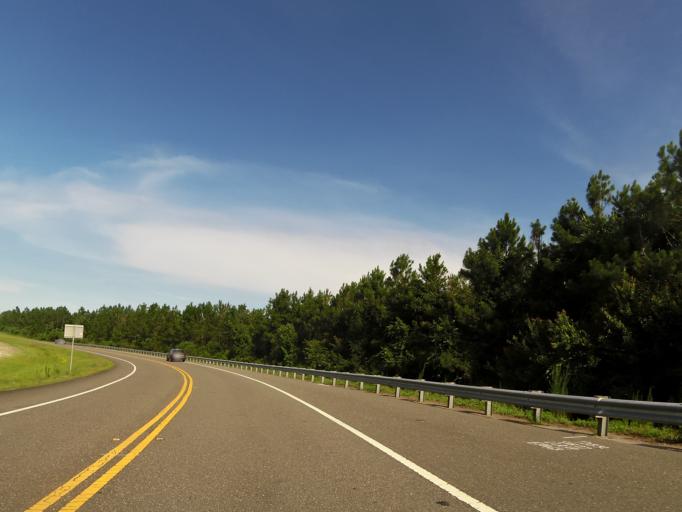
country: US
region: Florida
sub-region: Clay County
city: Green Cove Springs
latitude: 30.0137
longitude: -81.6038
